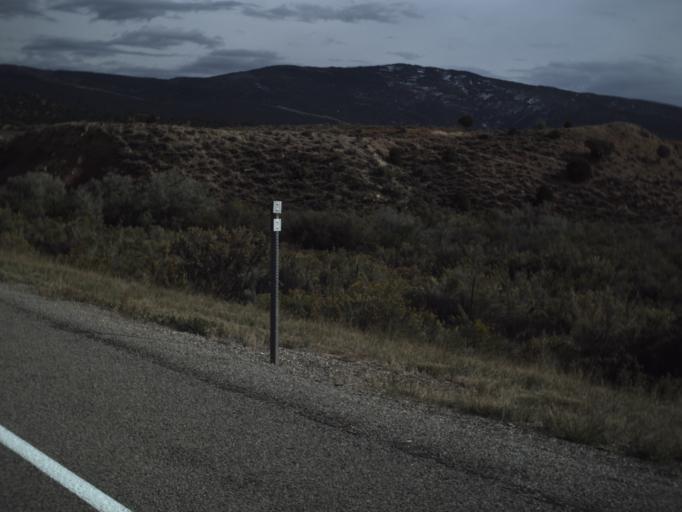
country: US
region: Utah
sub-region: Sevier County
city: Salina
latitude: 38.9169
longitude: -111.7450
